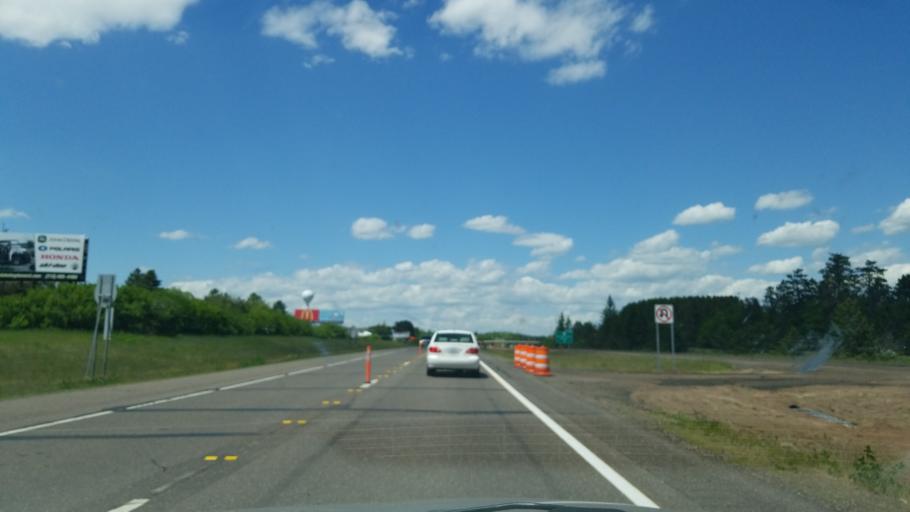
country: US
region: Minnesota
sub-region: Carlton County
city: Moose Lake
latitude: 46.3104
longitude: -92.8272
